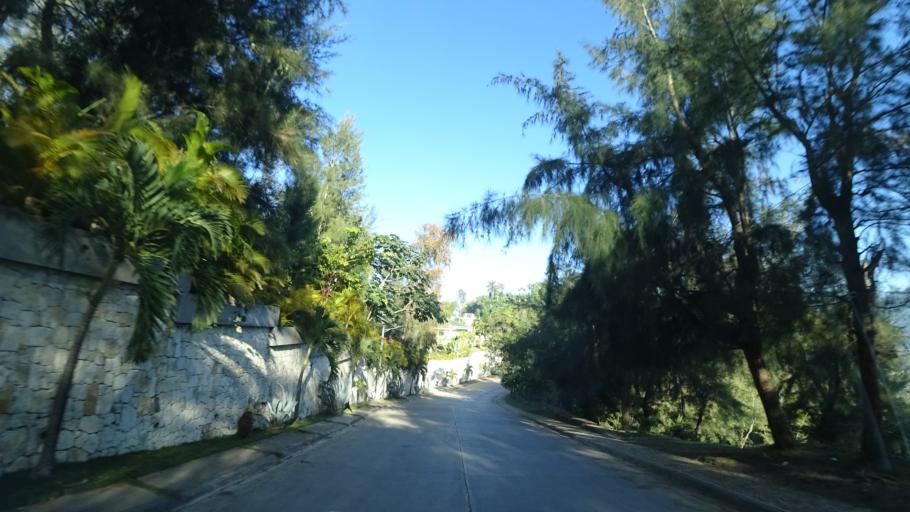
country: HT
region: Ouest
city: Port-au-Prince
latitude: 18.4987
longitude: -72.3511
